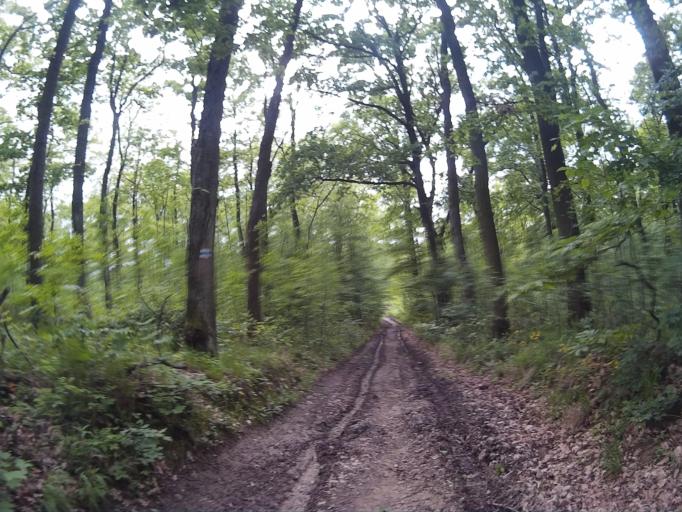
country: HU
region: Zala
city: Cserszegtomaj
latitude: 46.8588
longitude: 17.2319
